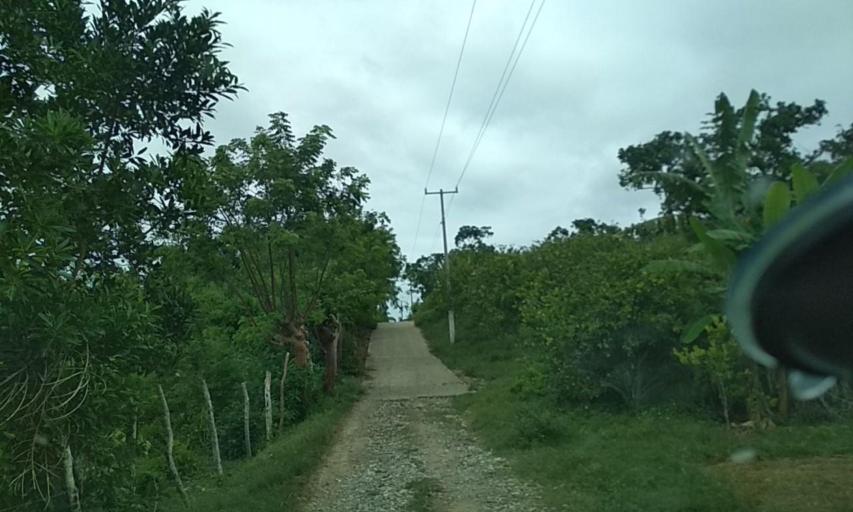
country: MX
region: Veracruz
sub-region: Papantla
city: Residencial Tajin
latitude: 20.6134
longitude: -97.3533
